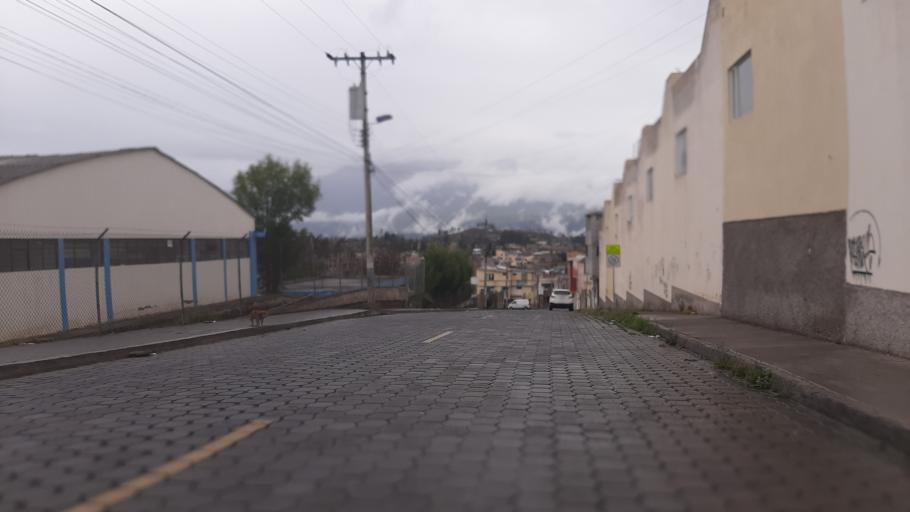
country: EC
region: Chimborazo
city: Riobamba
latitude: -1.6550
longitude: -78.6430
